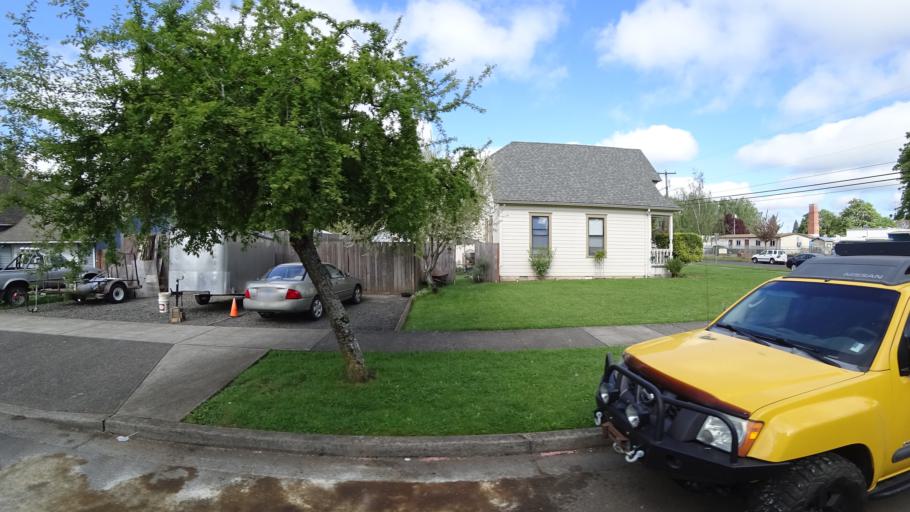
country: US
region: Oregon
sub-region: Washington County
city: Hillsboro
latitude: 45.5172
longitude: -122.9827
